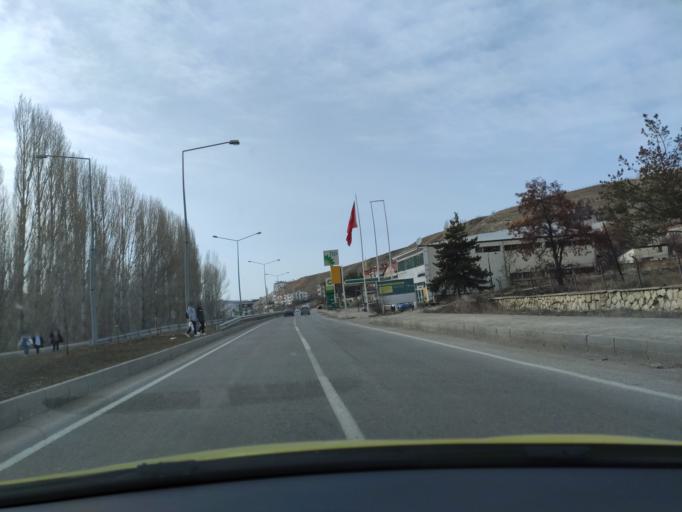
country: TR
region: Bayburt
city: Bayburt
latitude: 40.2415
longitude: 40.2456
